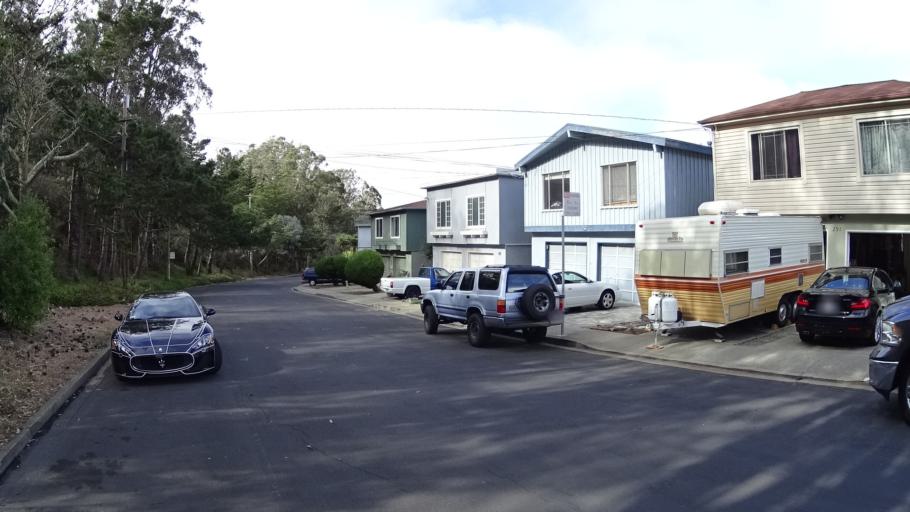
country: US
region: California
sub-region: San Mateo County
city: Daly City
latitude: 37.7030
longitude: -122.4281
